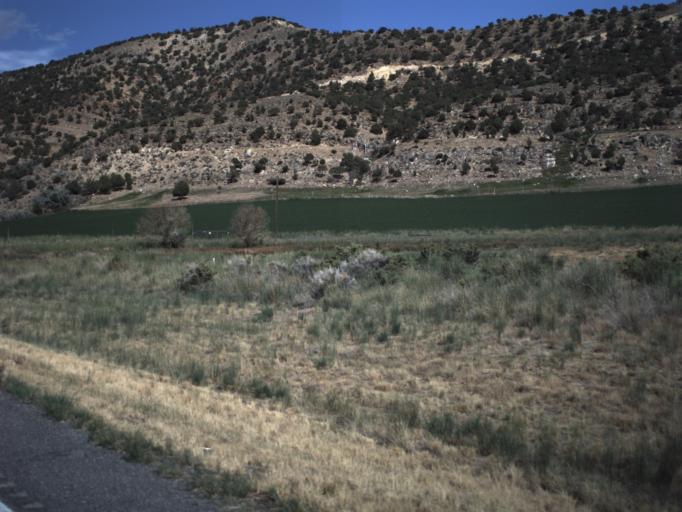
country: US
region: Utah
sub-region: Sanpete County
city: Manti
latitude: 39.2337
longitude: -111.6633
